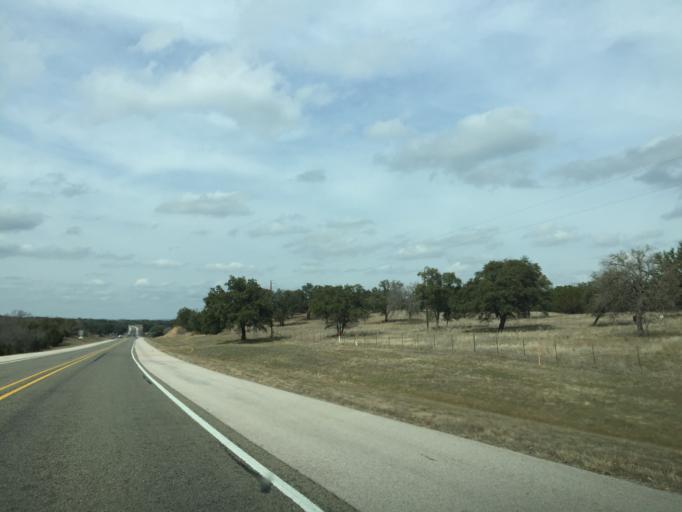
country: US
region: Texas
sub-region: Burnet County
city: Granite Shoals
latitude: 30.5338
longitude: -98.4390
